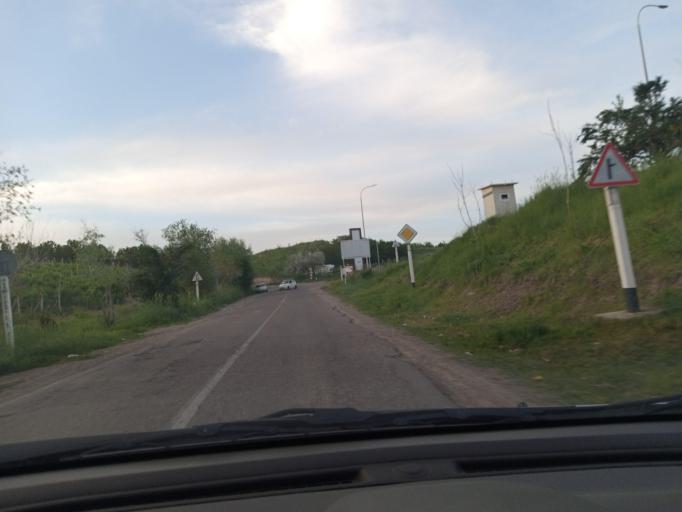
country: UZ
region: Toshkent
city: Parkent
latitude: 41.2462
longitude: 69.7333
